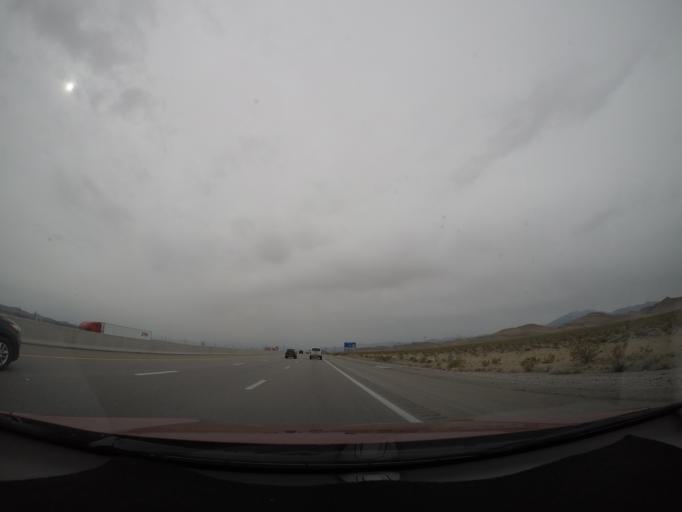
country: US
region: Nevada
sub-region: Clark County
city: Sandy Valley
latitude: 35.6357
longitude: -115.3846
